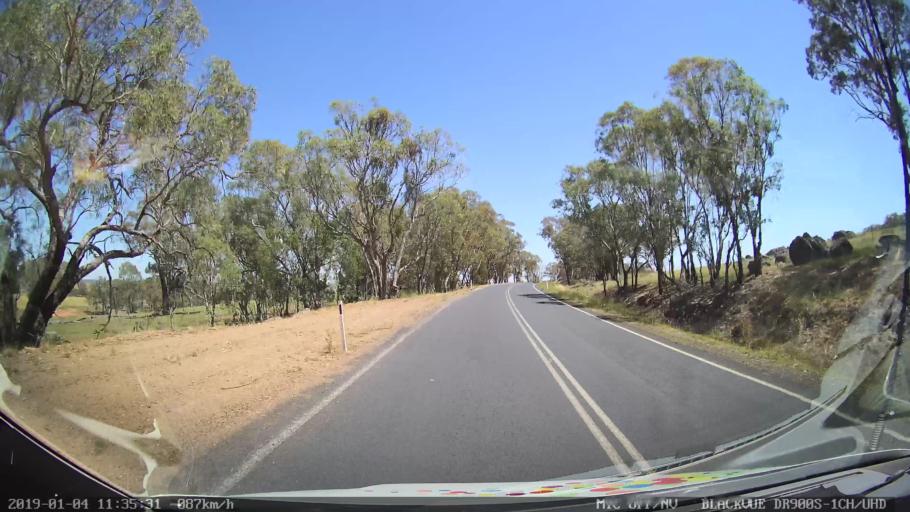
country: AU
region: New South Wales
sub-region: Cabonne
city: Molong
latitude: -33.0554
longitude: 148.8195
